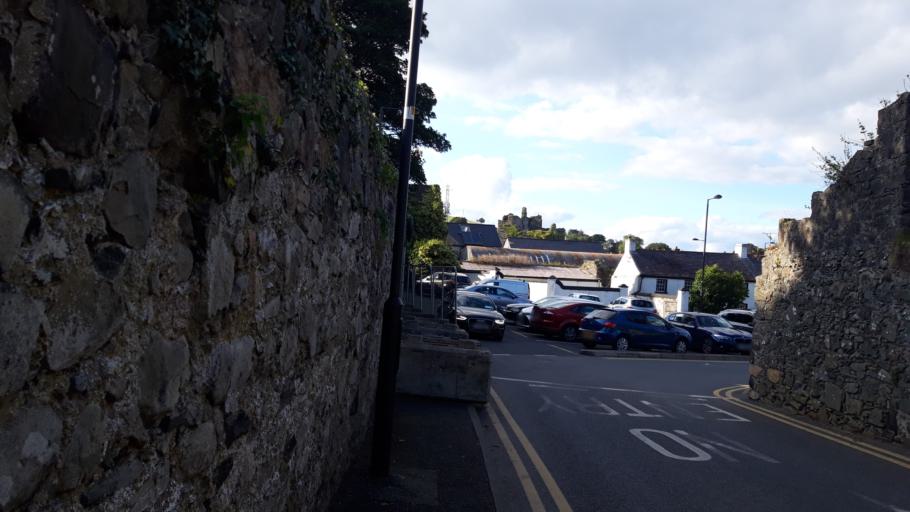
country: IE
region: Leinster
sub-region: Lu
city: Carlingford
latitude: 54.0395
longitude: -6.1849
